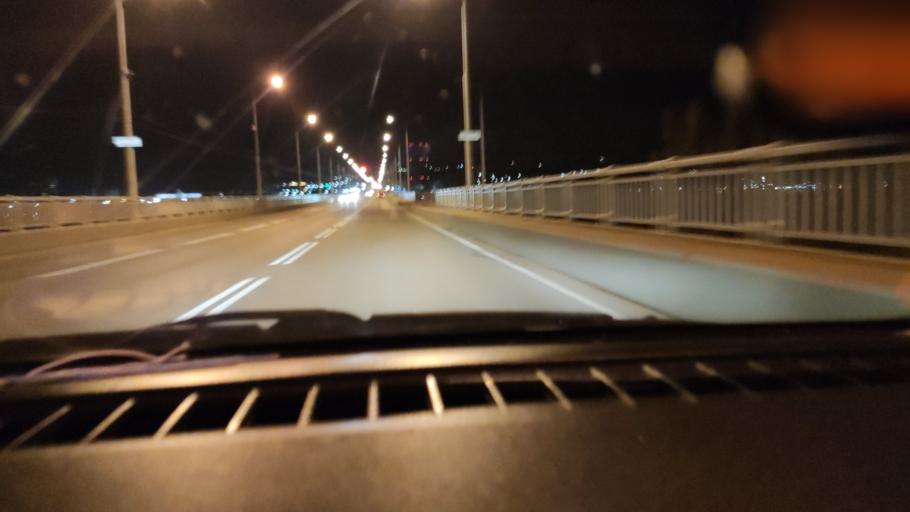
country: RU
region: Saratov
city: Engel's
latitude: 51.5154
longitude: 46.0716
